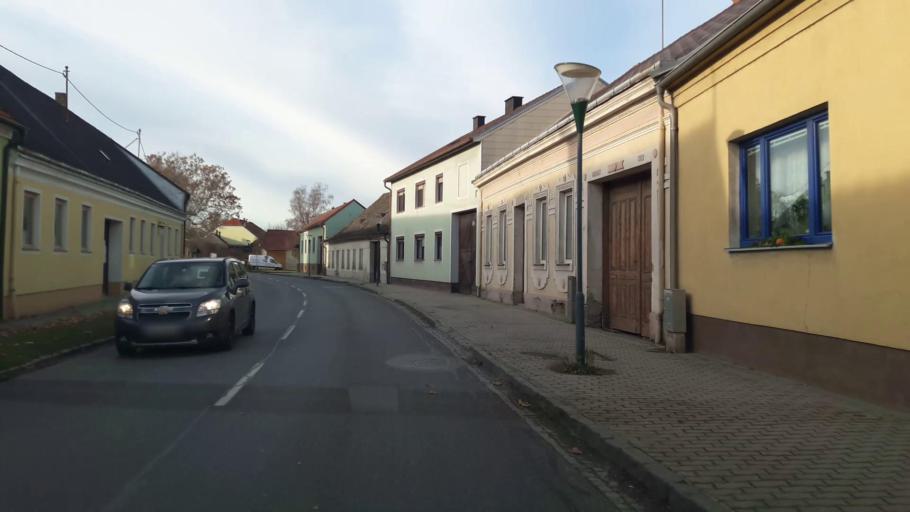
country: AT
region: Lower Austria
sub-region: Politischer Bezirk Ganserndorf
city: Bad Pirawarth
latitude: 48.4506
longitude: 16.6034
